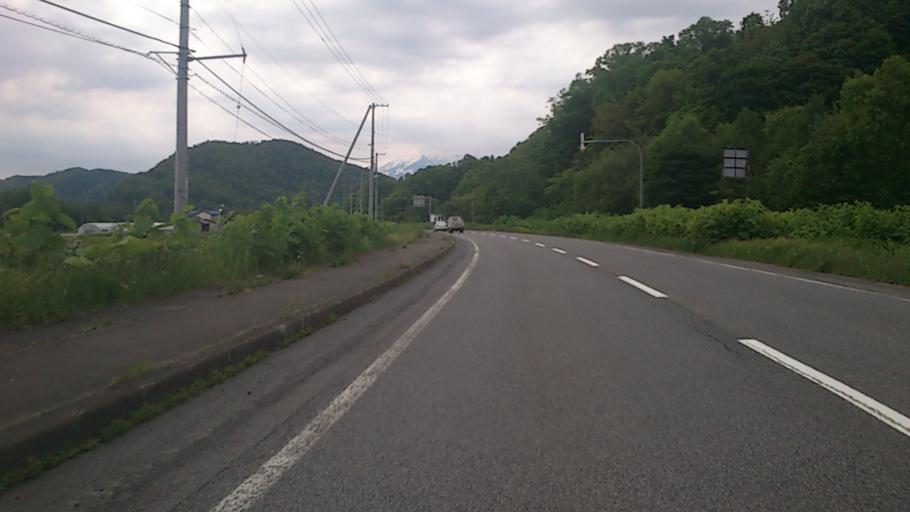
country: JP
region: Hokkaido
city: Kamikawa
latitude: 43.8472
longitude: 142.6963
